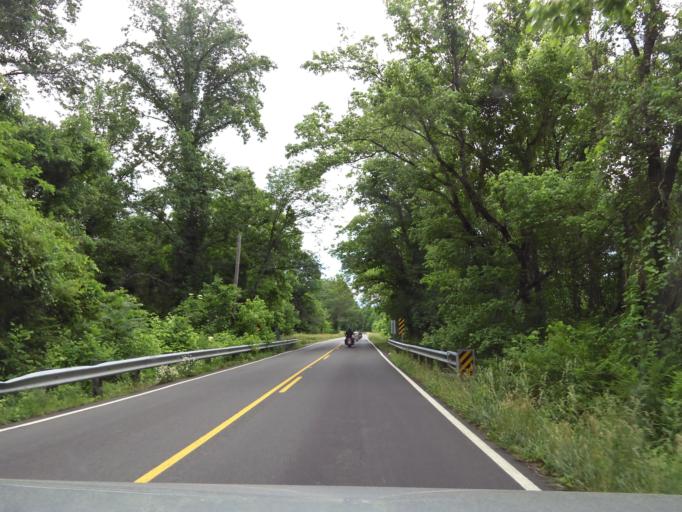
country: US
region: Tennessee
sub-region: Loudon County
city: Greenback
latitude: 35.5472
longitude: -84.0642
